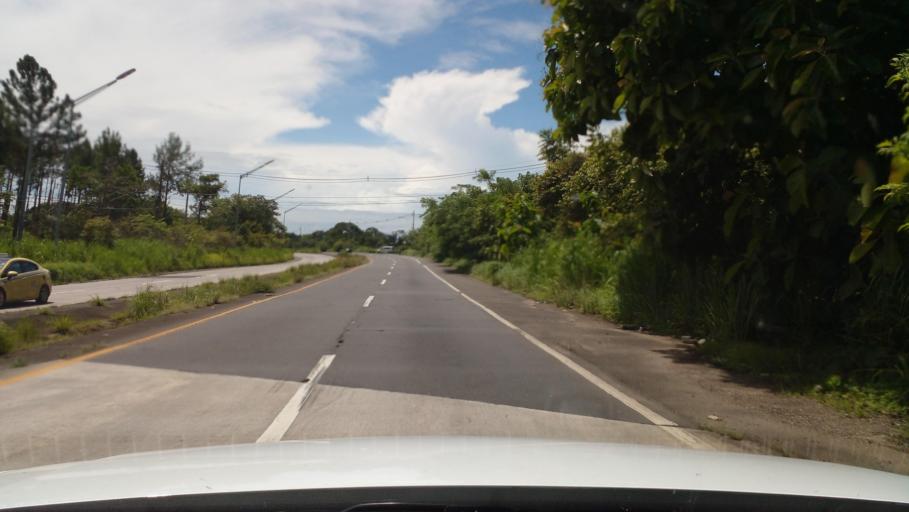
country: PA
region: Cocle
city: Rio Hato
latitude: 8.3830
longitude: -80.1204
